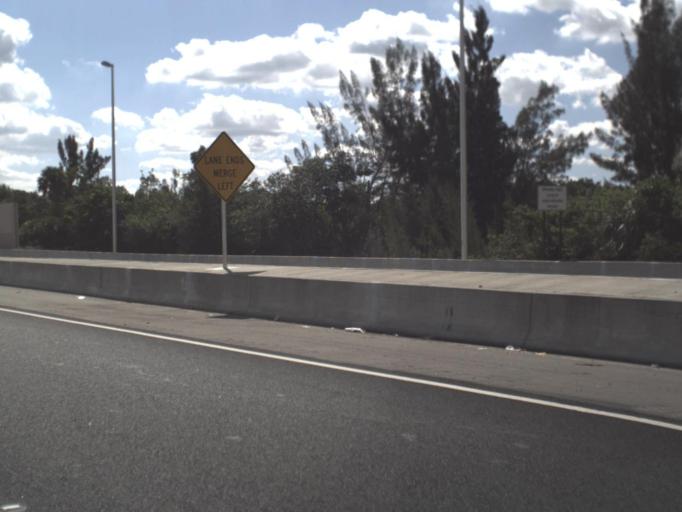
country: US
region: Florida
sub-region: Broward County
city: Davie
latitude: 26.0752
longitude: -80.2160
